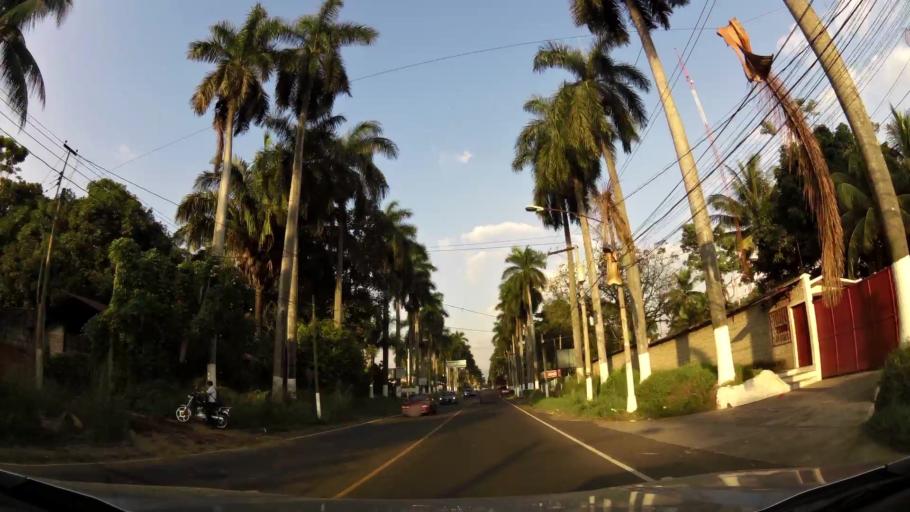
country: GT
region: Retalhuleu
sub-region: Municipio de Retalhuleu
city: Retalhuleu
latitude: 14.5410
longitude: -91.6715
